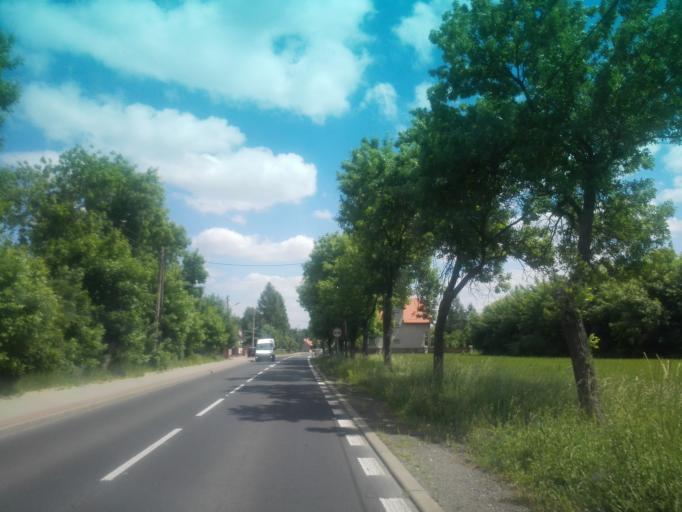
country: PL
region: Silesian Voivodeship
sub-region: Powiat czestochowski
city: Potok Zloty
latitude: 50.7237
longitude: 19.4267
